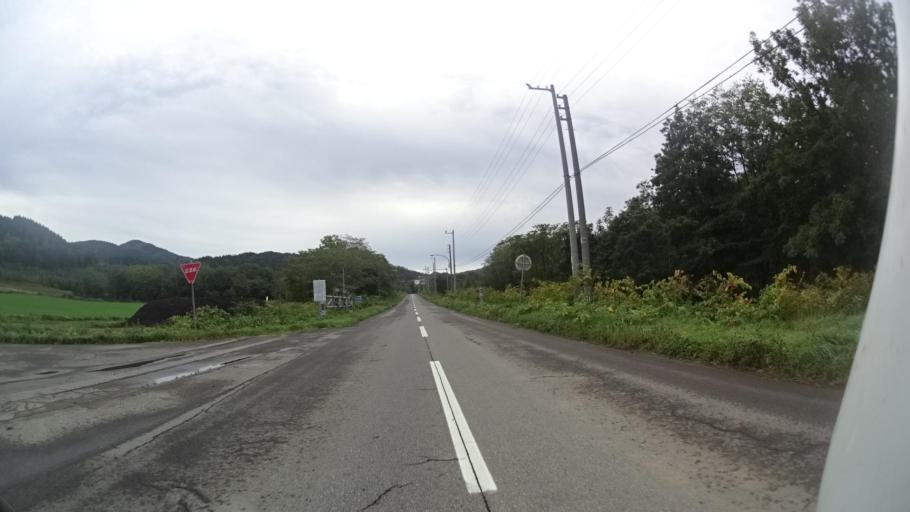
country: JP
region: Hokkaido
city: Shibetsu
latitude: 43.8434
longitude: 144.7844
